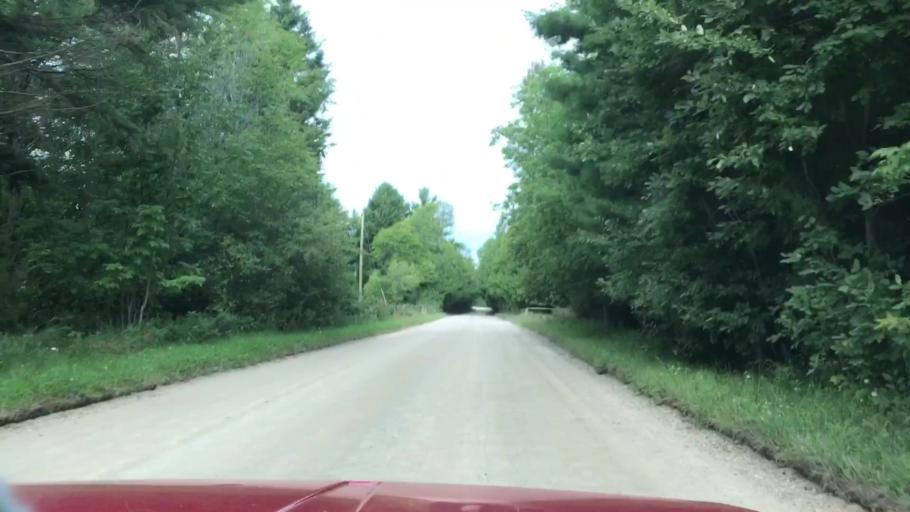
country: US
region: Michigan
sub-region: Charlevoix County
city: Charlevoix
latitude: 45.7280
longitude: -85.5375
